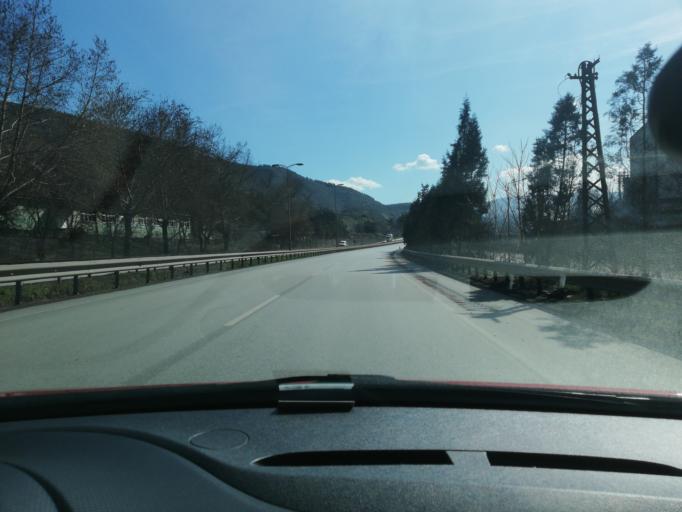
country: TR
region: Karabuk
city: Karabuk
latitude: 41.1868
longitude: 32.6386
